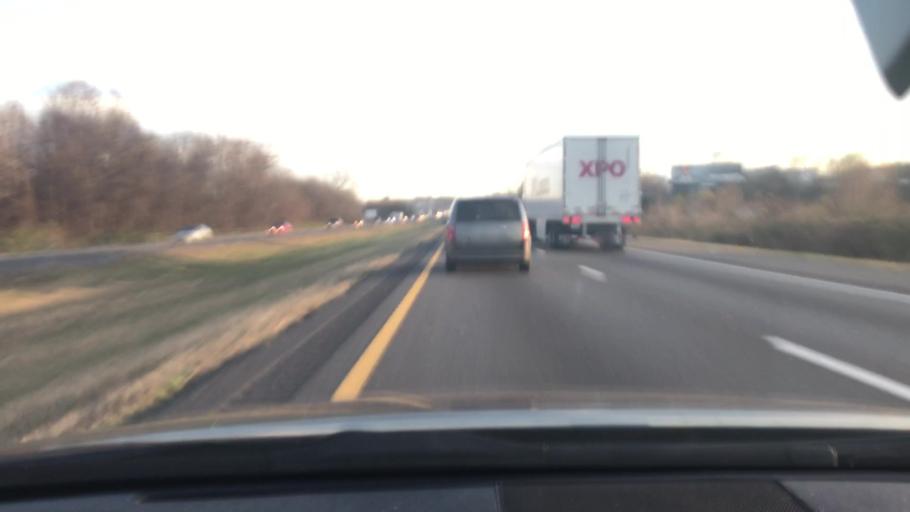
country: US
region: Tennessee
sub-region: Davidson County
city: Goodlettsville
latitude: 36.3383
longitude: -86.7123
